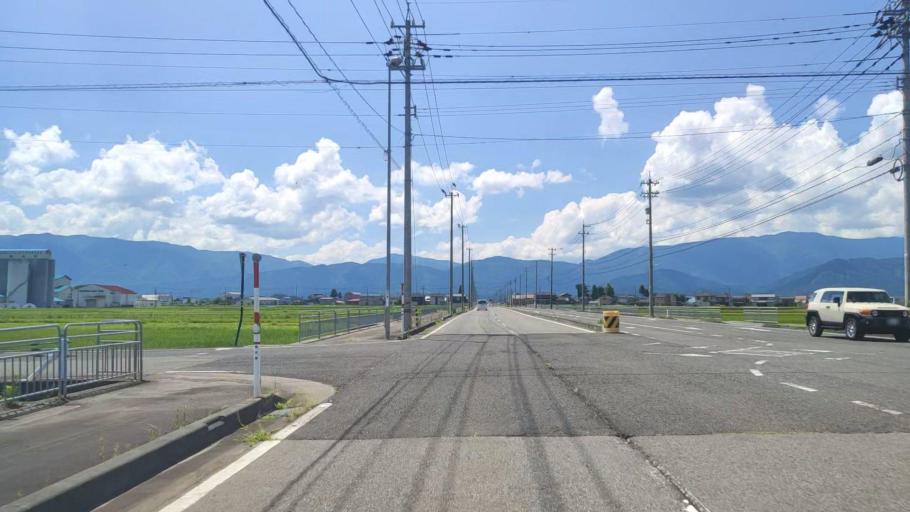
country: JP
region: Fukui
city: Ono
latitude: 35.9940
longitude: 136.5096
